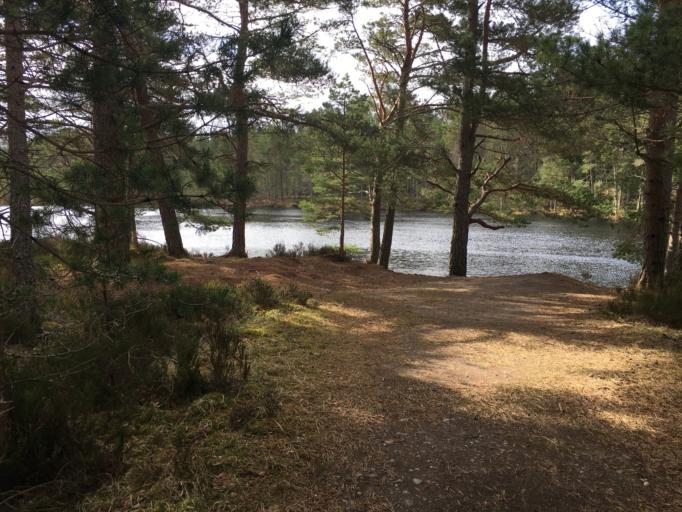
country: GB
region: Scotland
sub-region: Highland
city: Kingussie
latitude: 57.0957
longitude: -3.9252
